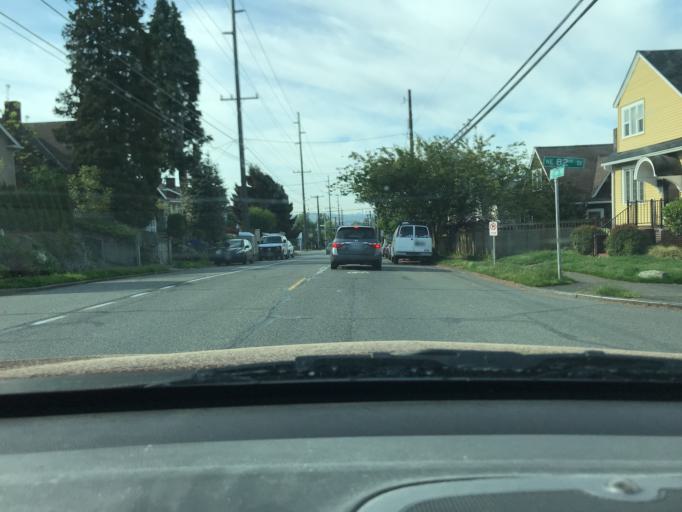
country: US
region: Washington
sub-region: King County
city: Shoreline
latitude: 47.6884
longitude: -122.3230
